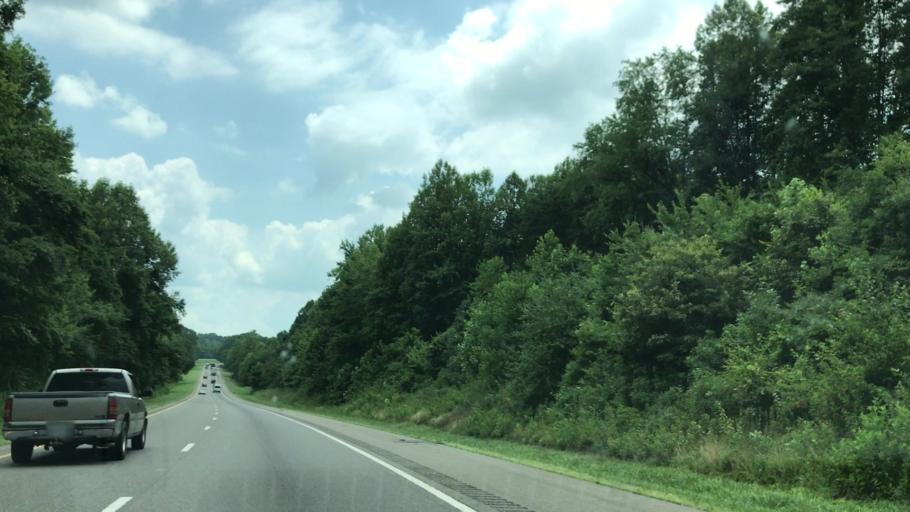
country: US
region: North Carolina
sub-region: Surry County
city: Dobson
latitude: 36.4362
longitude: -80.7786
